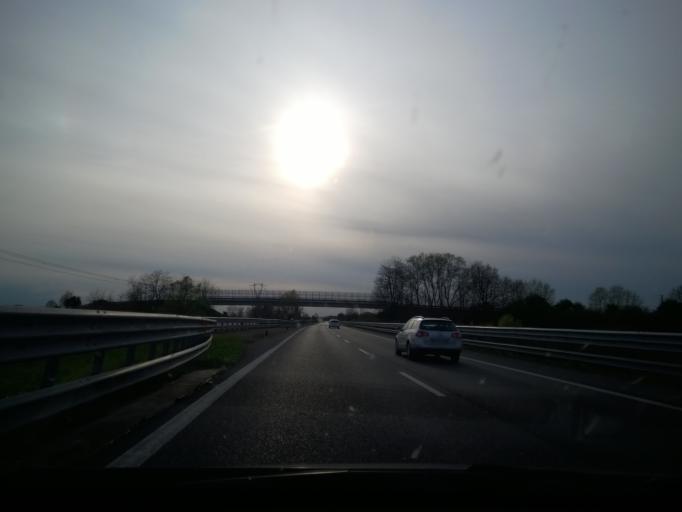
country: IT
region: Emilia-Romagna
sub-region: Provincia di Piacenza
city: Monticelli d'Ongina
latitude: 45.0594
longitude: 9.9320
